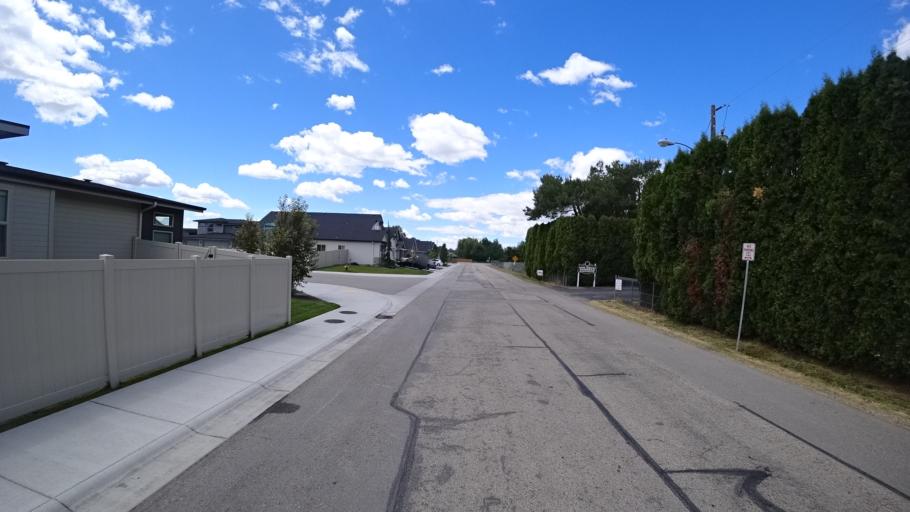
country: US
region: Idaho
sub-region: Ada County
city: Eagle
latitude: 43.6447
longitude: -116.3425
